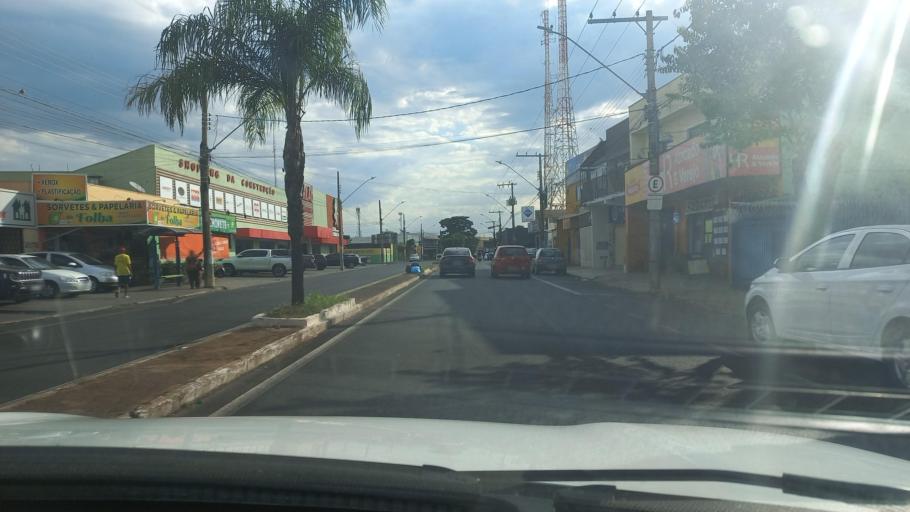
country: BR
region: Minas Gerais
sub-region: Uberaba
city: Uberaba
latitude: -19.7666
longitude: -47.9206
